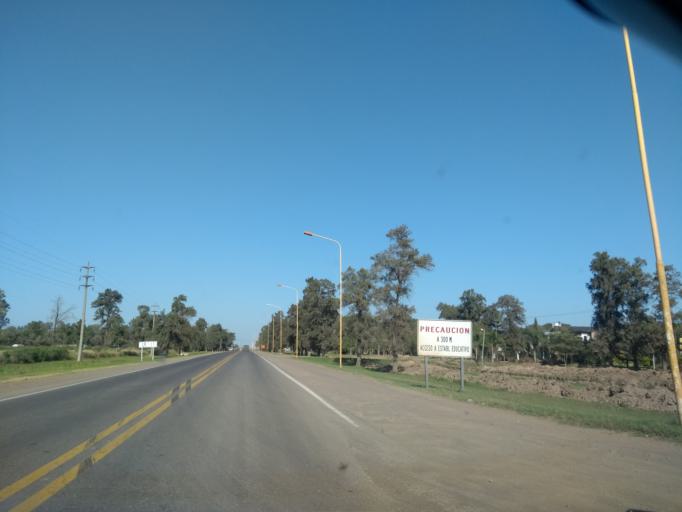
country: AR
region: Chaco
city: Presidencia Roque Saenz Pena
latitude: -26.8043
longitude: -60.4148
